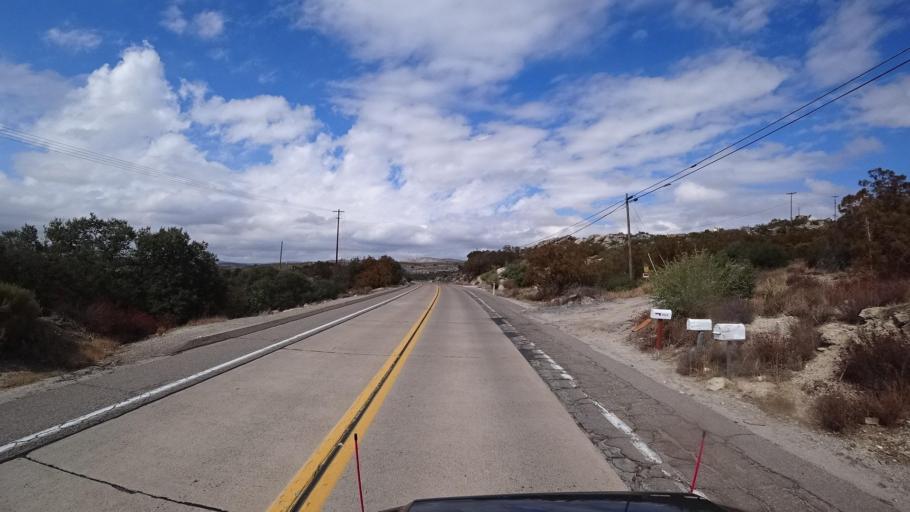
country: US
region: California
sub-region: San Diego County
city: Campo
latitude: 32.6756
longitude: -116.3280
